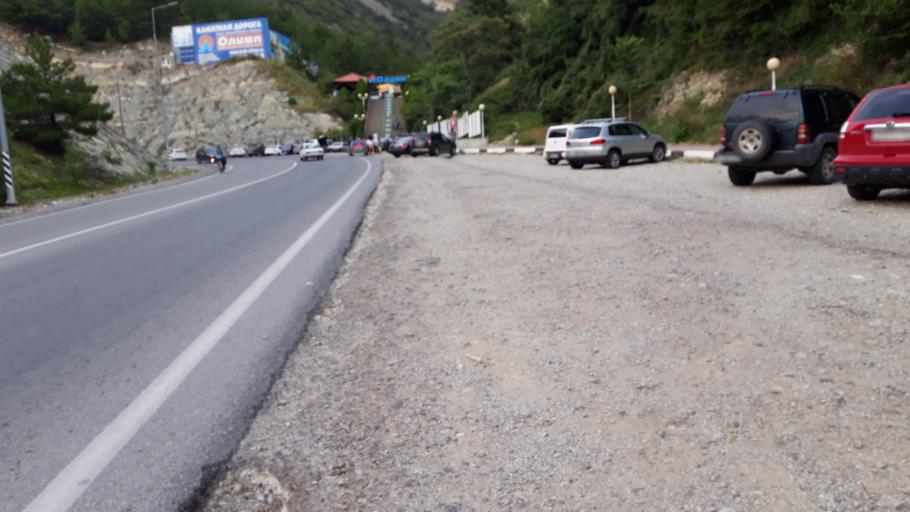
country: RU
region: Krasnodarskiy
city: Gelendzhik
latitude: 44.5760
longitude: 38.0925
